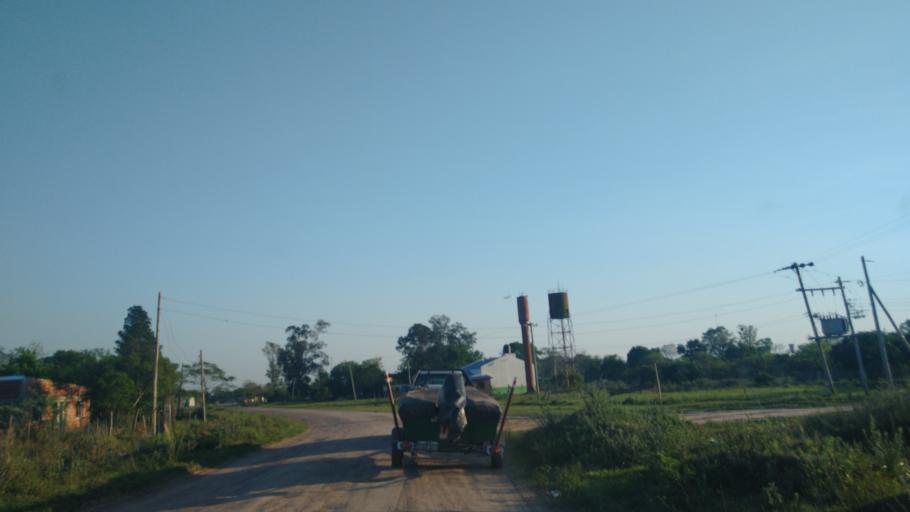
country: PY
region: Neembucu
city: Cerrito
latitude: -27.3754
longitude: -57.6548
